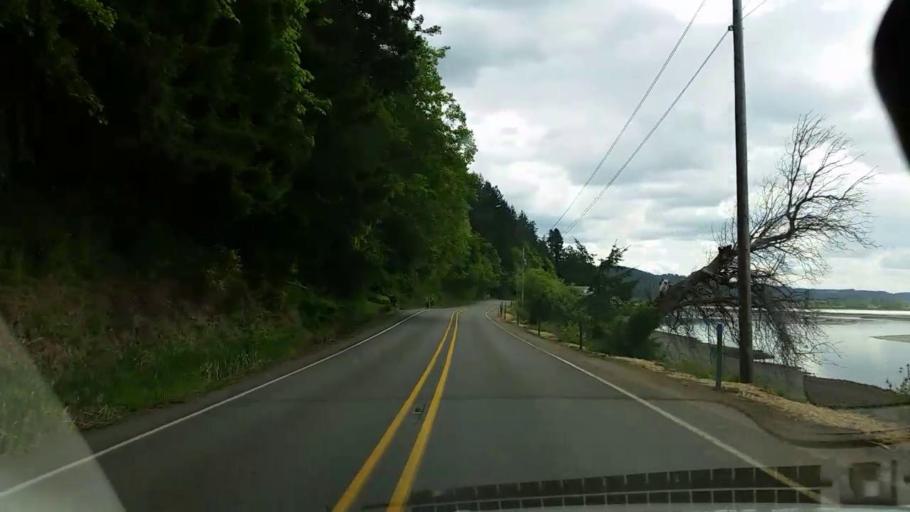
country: US
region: Washington
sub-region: Mason County
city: Shelton
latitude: 47.3517
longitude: -123.1066
